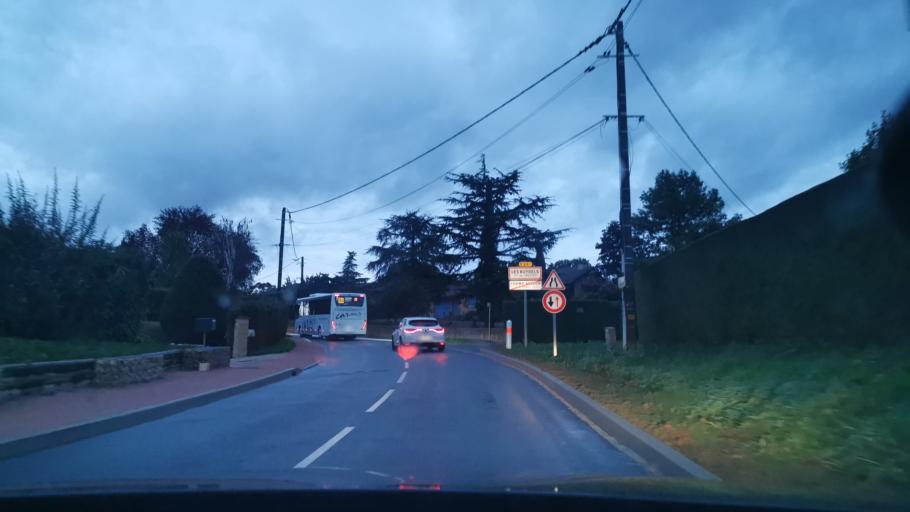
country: FR
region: Rhone-Alpes
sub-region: Departement de l'Ain
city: Crottet
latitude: 46.2705
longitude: 4.8986
